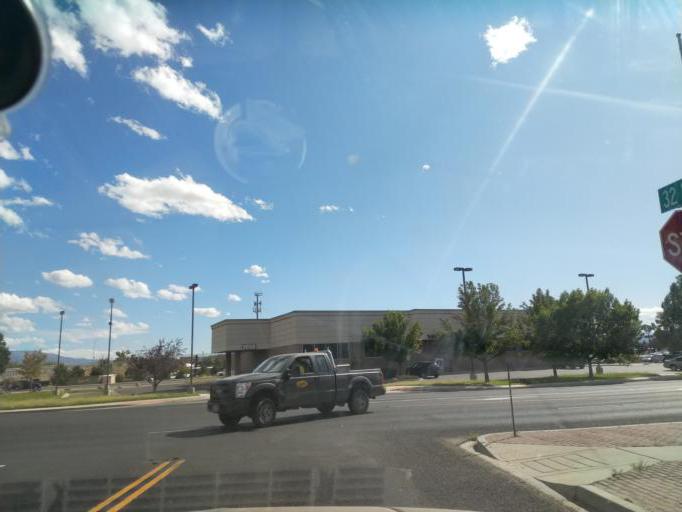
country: US
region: Colorado
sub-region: Mesa County
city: Clifton
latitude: 39.0885
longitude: -108.4594
